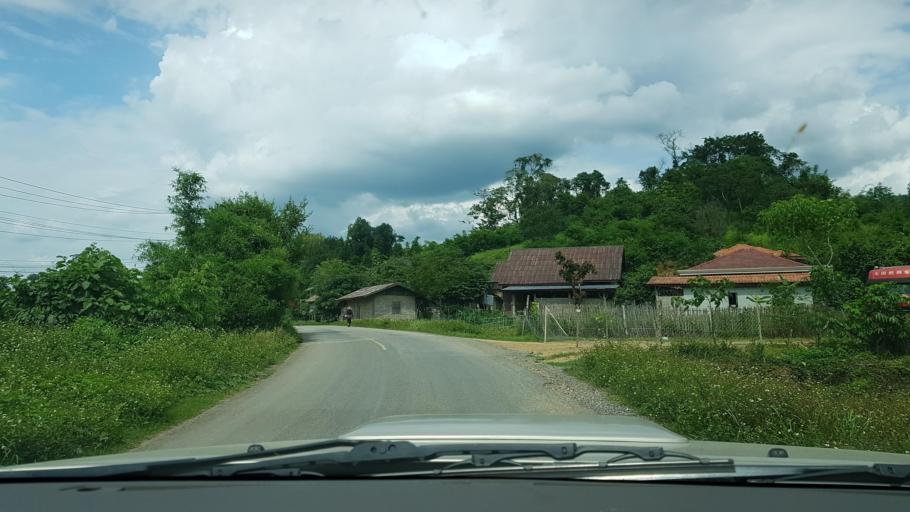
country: LA
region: Loungnamtha
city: Muang Nale
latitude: 20.2506
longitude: 101.5824
